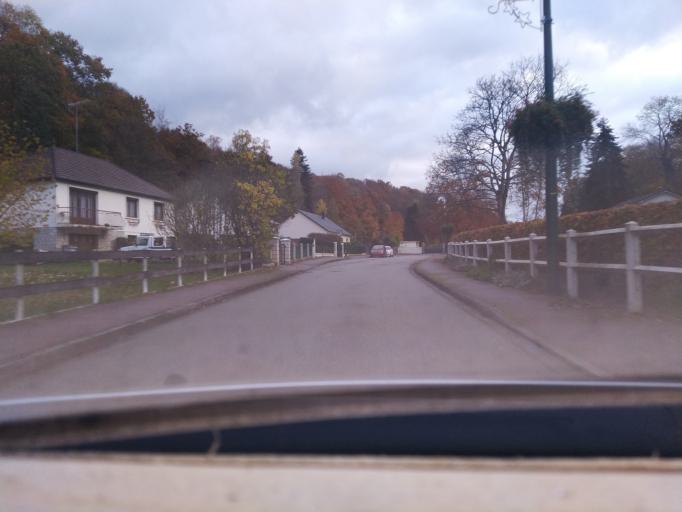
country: FR
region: Haute-Normandie
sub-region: Departement de la Seine-Maritime
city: Yainville
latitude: 49.4532
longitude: 0.8322
